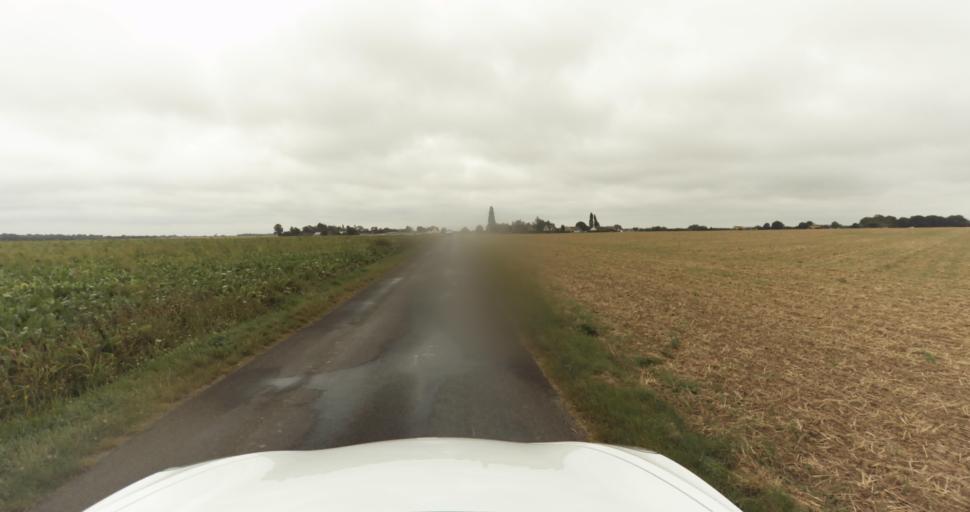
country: FR
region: Haute-Normandie
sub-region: Departement de l'Eure
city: Aviron
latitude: 49.0742
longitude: 1.0709
